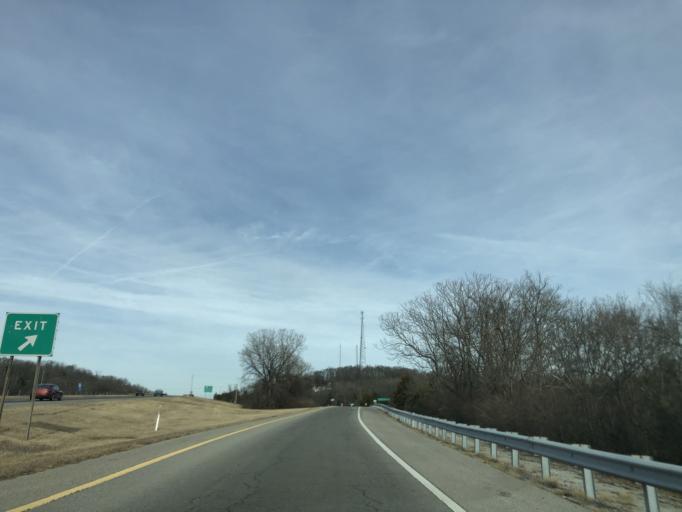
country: US
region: Tennessee
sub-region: Davidson County
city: Nashville
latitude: 36.2157
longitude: -86.7477
